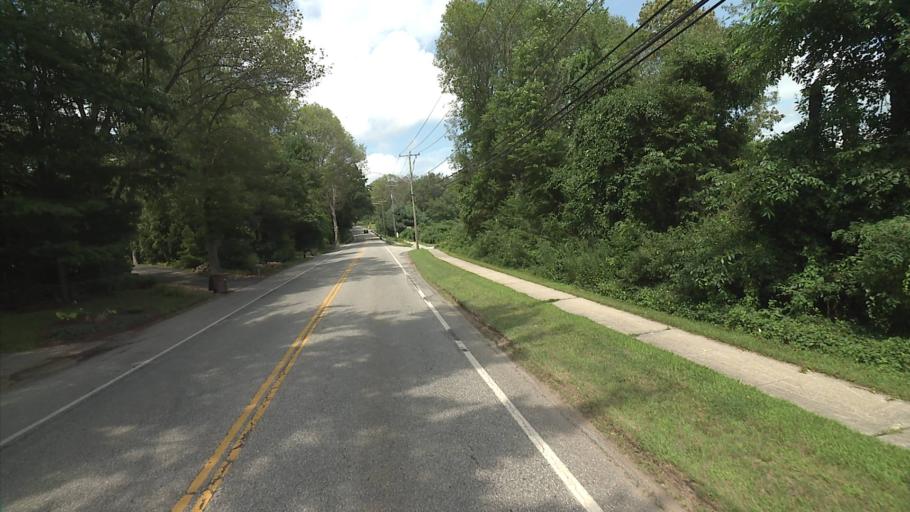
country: US
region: Connecticut
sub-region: New London County
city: Niantic
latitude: 41.3731
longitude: -72.2118
